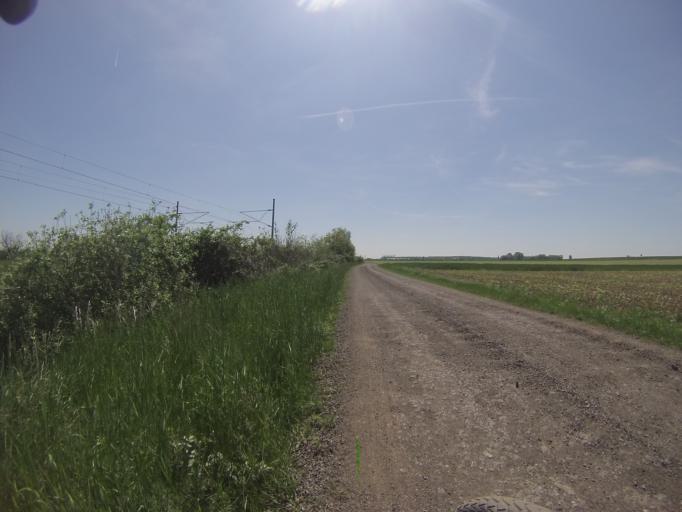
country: CZ
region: South Moravian
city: Vranovice
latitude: 48.9826
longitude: 16.5990
